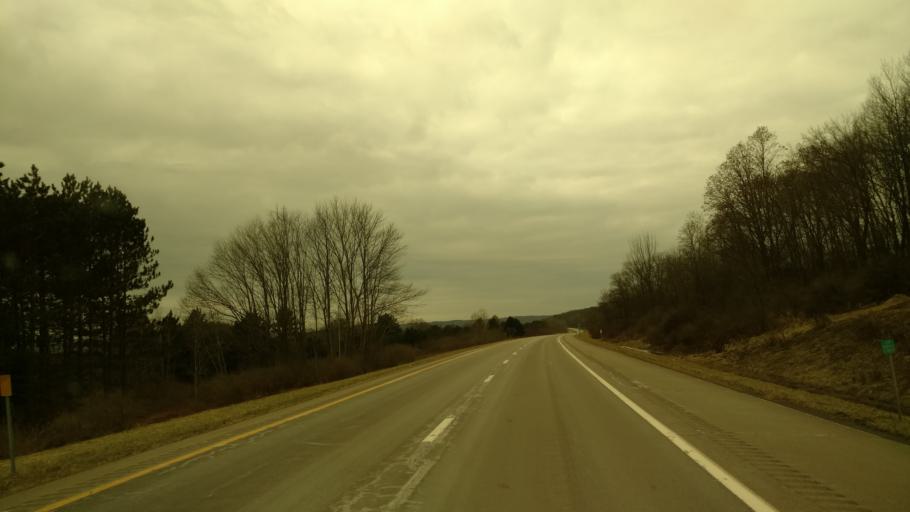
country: US
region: New York
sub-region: Chautauqua County
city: Falconer
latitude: 42.1354
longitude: -79.1450
